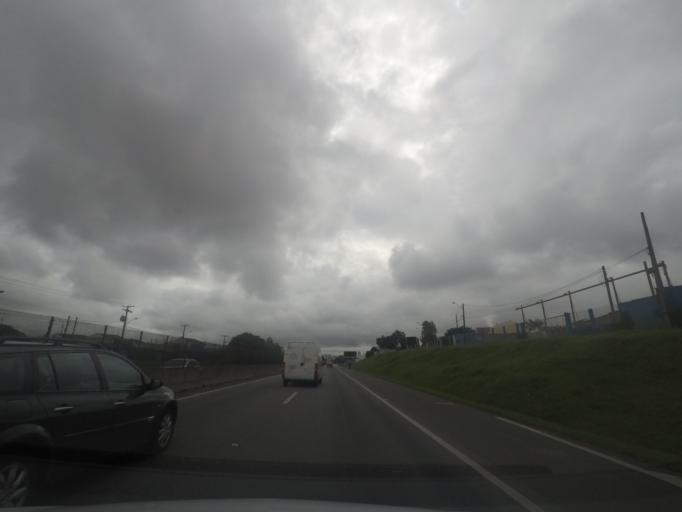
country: BR
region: Parana
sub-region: Pinhais
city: Pinhais
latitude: -25.4623
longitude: -49.2185
